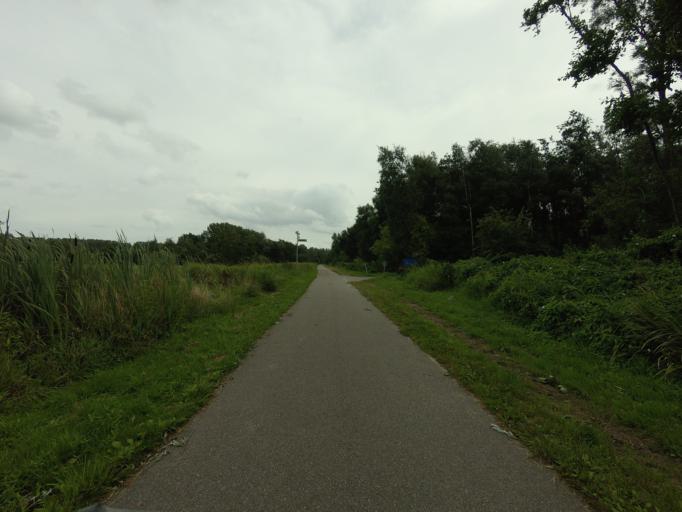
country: NL
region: North Holland
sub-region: Gemeente Amsterdam
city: Driemond
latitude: 52.3223
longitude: 5.0089
